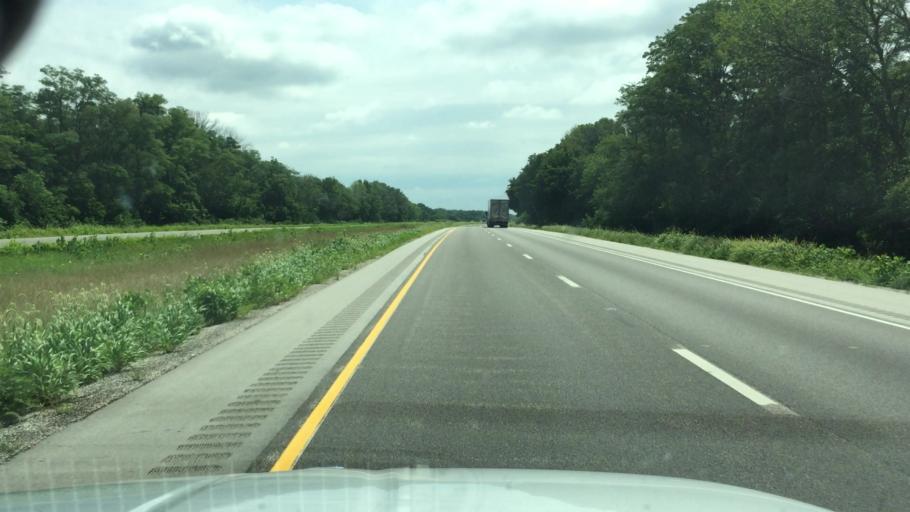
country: US
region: Illinois
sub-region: Peoria County
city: Elmwood
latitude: 40.8671
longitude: -90.0309
